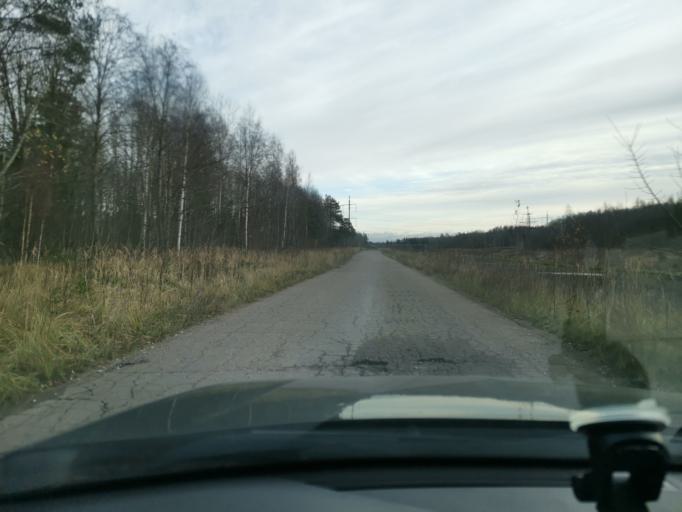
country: EE
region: Ida-Virumaa
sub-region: Sillamaee linn
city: Sillamae
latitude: 59.2649
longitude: 27.9002
